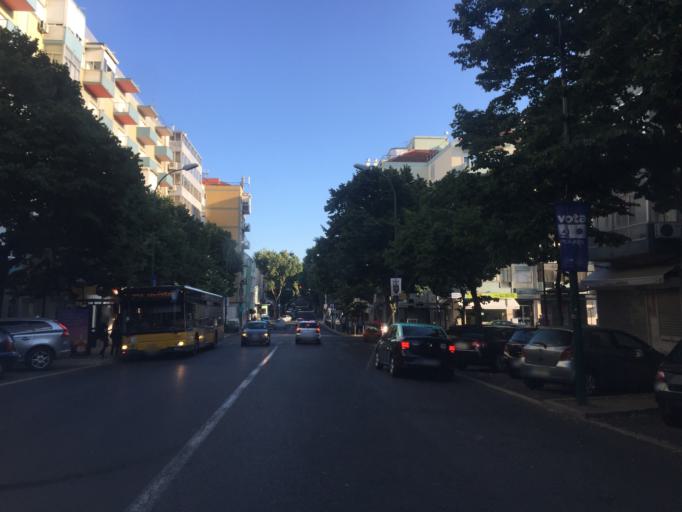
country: PT
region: Lisbon
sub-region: Odivelas
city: Pontinha
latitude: 38.7517
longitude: -9.1974
